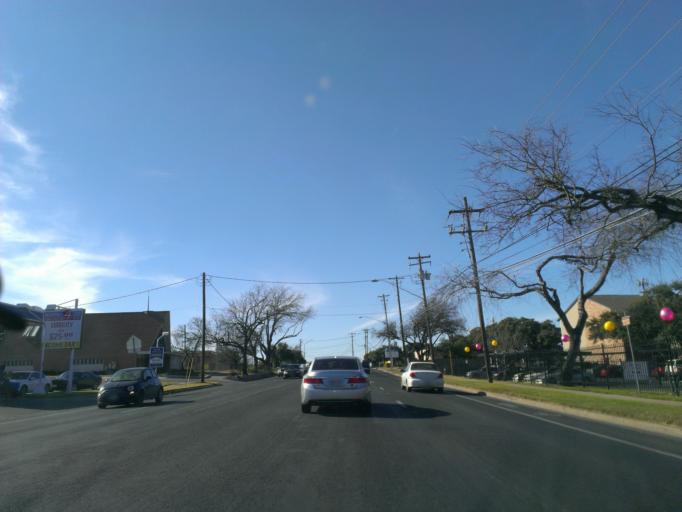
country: US
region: Texas
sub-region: Travis County
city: Austin
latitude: 30.2327
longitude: -97.7378
